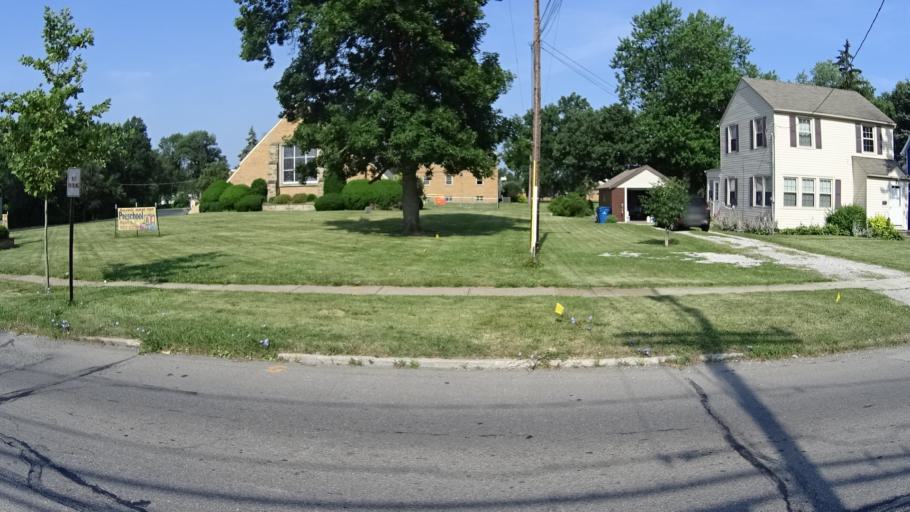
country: US
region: Ohio
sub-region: Lorain County
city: Vermilion
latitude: 41.4162
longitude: -82.3656
